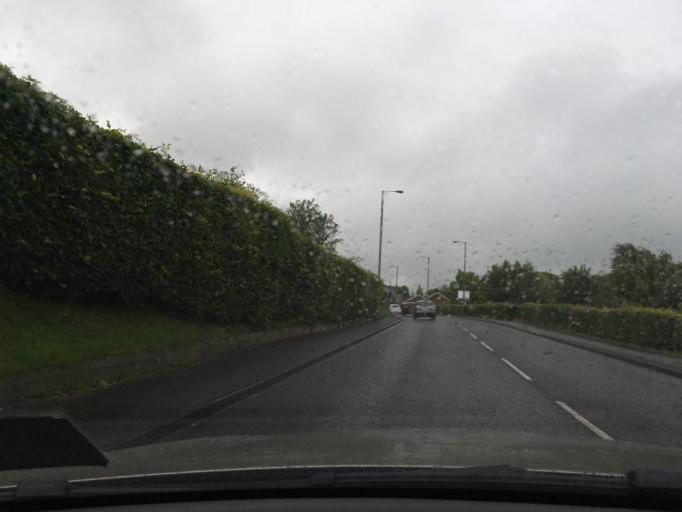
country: GB
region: Northern Ireland
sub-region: Fermanagh District
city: Enniskillen
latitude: 54.3510
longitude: -7.6380
